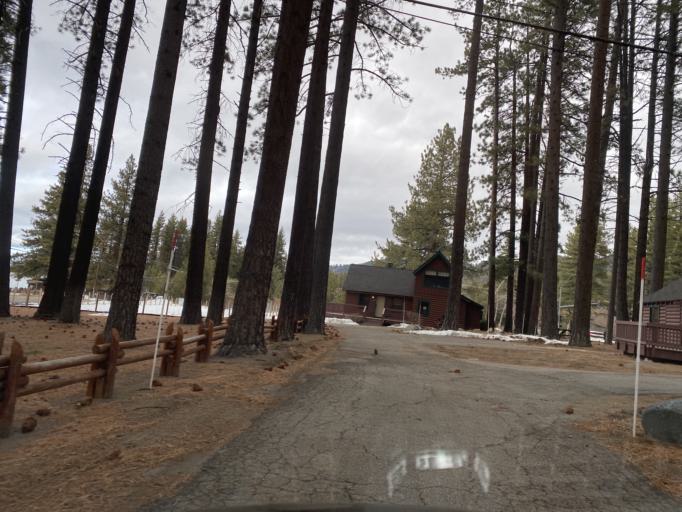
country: US
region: Nevada
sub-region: Douglas County
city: Kingsbury
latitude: 39.0056
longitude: -119.9480
